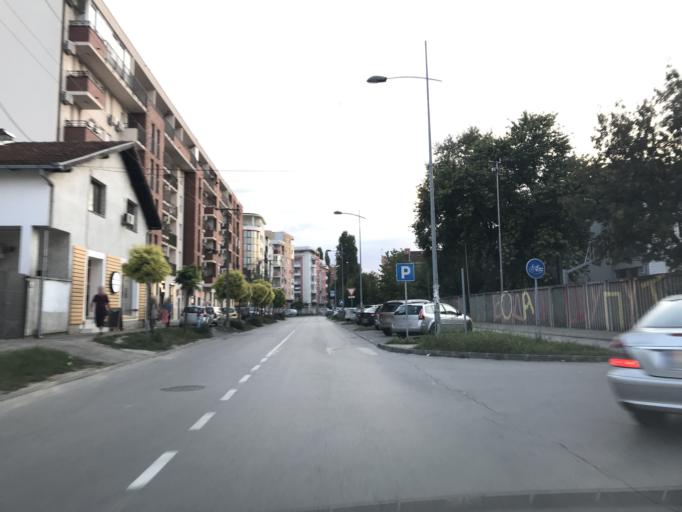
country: RS
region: Autonomna Pokrajina Vojvodina
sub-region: Juznobacki Okrug
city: Novi Sad
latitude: 45.2611
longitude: 19.8156
